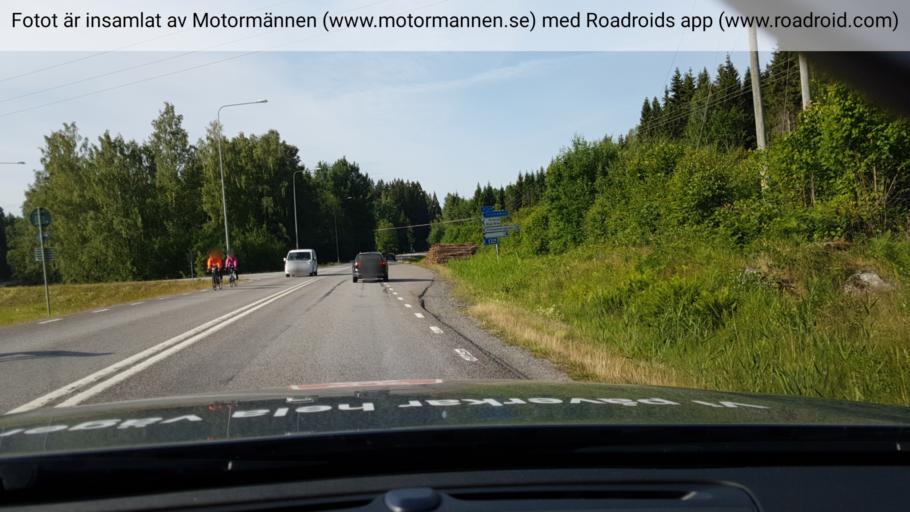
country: SE
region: OErebro
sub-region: Askersunds Kommun
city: Askersund
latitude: 58.7648
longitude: 14.7977
